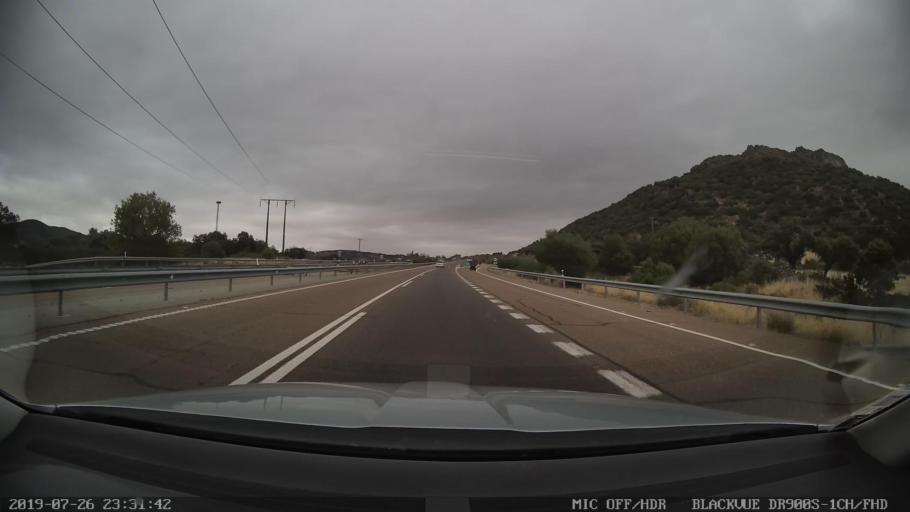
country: ES
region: Extremadura
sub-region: Provincia de Caceres
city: Puerto de Santa Cruz
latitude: 39.3041
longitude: -5.8571
